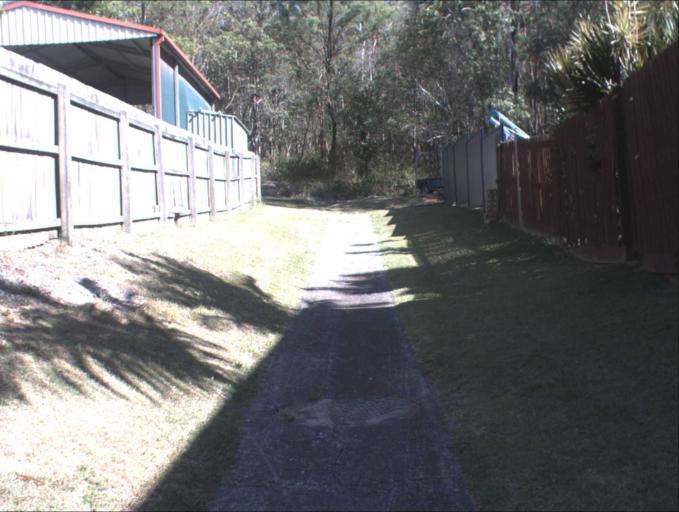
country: AU
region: Queensland
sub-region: Logan
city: Windaroo
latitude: -27.7272
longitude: 153.1862
